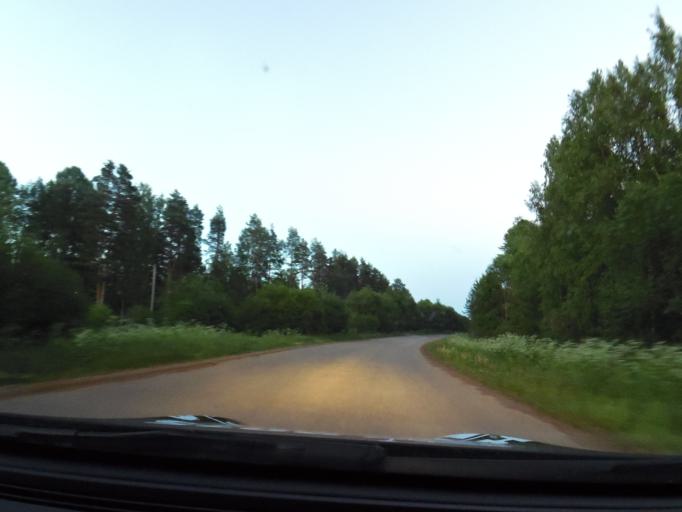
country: RU
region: Vologda
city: Vytegra
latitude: 61.0025
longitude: 36.3103
